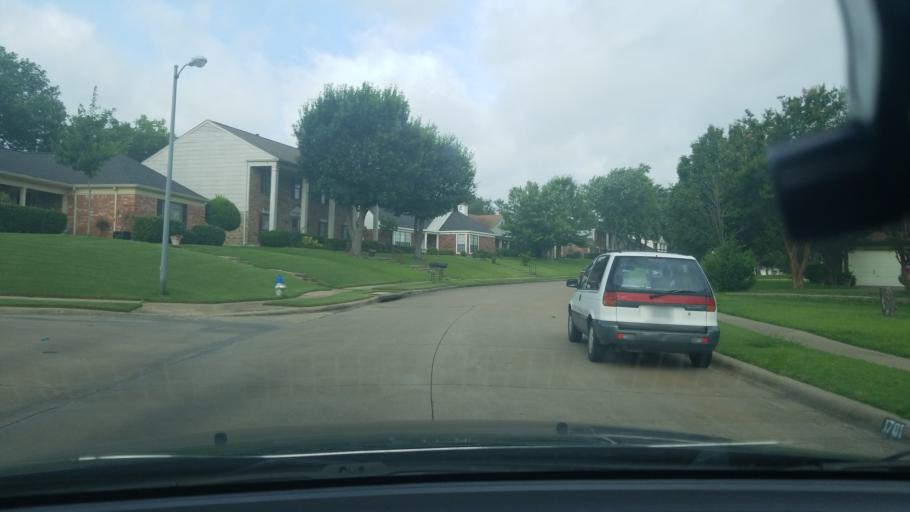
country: US
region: Texas
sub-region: Dallas County
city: Mesquite
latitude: 32.7894
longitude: -96.6477
